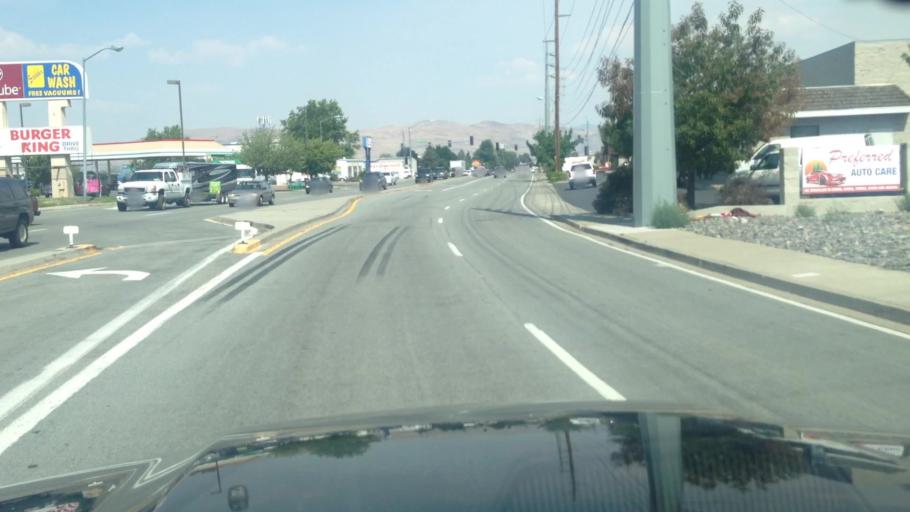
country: US
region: Nevada
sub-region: Washoe County
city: Sparks
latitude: 39.5234
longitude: -119.7690
